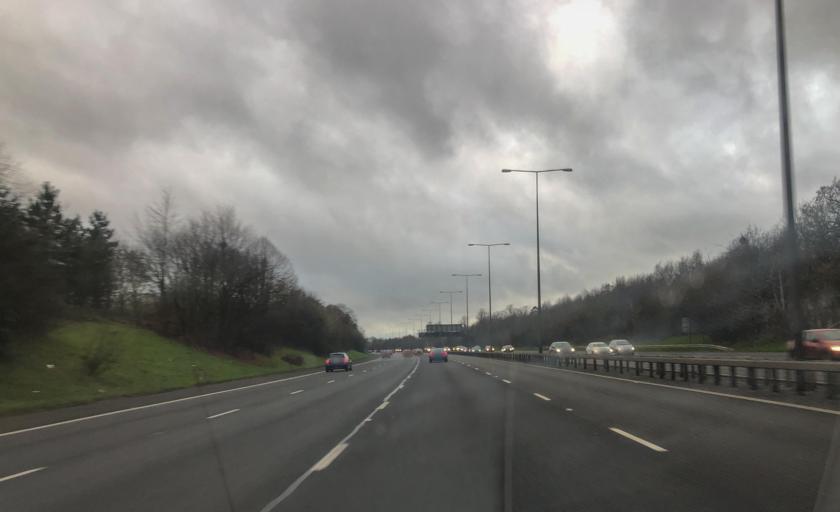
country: GB
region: England
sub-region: Buckinghamshire
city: Beaconsfield
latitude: 51.5978
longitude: -0.6441
